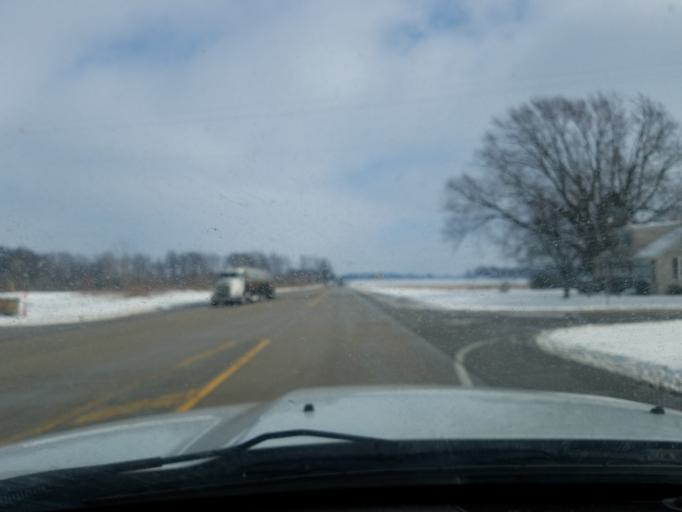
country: US
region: Indiana
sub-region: Marshall County
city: Plymouth
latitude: 41.4498
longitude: -86.2864
